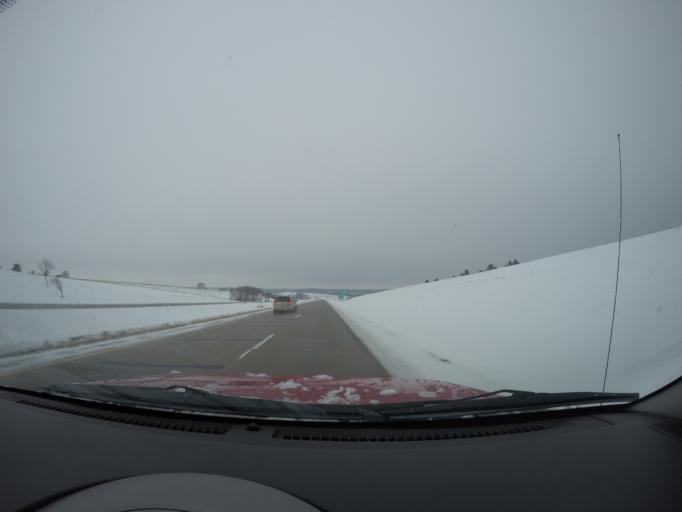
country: US
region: Minnesota
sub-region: Olmsted County
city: Rochester
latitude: 43.9741
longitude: -92.4259
